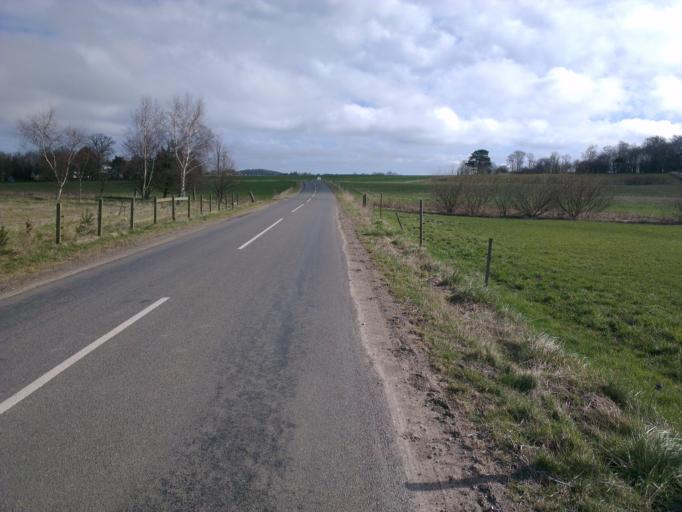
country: DK
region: Capital Region
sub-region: Hillerod Kommune
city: Skaevinge
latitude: 55.8746
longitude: 12.1183
